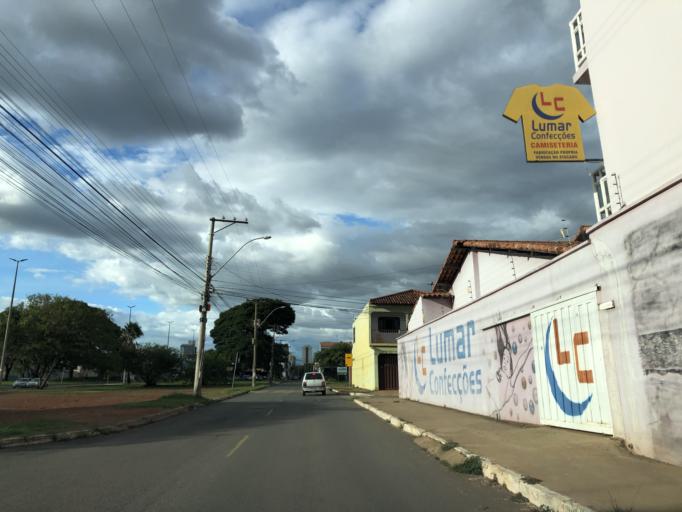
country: BR
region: Goias
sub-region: Luziania
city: Luziania
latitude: -16.0279
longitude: -48.0602
